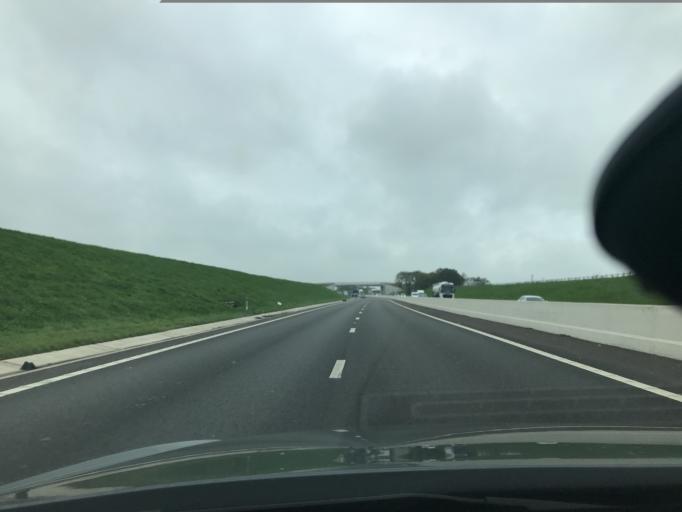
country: GB
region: England
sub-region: Cheshire East
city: Mere
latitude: 53.3504
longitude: -2.4072
